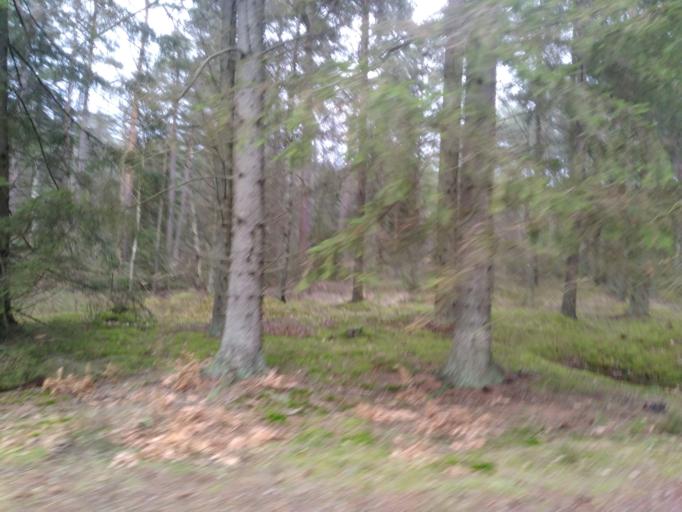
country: SE
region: Vaestra Goetaland
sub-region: Lidkopings Kommun
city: Lidkoping
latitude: 58.4863
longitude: 13.1599
